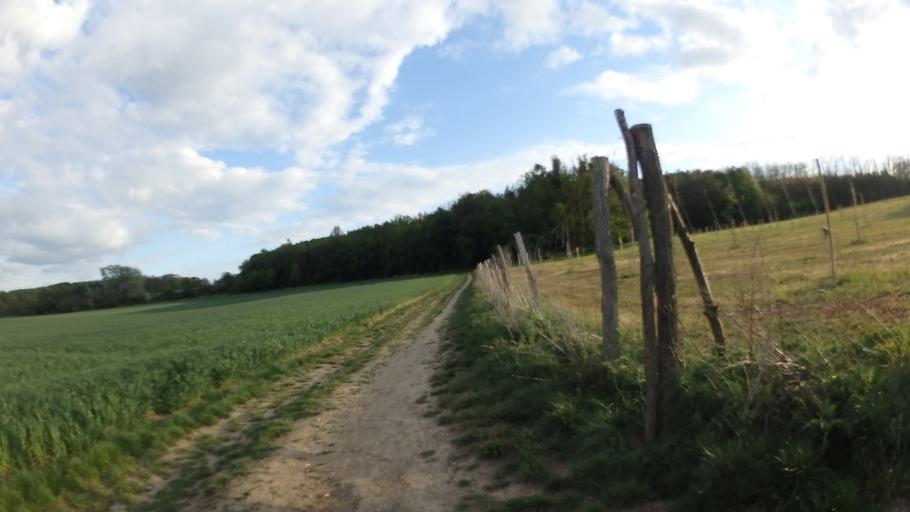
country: CZ
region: South Moravian
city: Moravany
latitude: 49.1369
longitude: 16.5690
